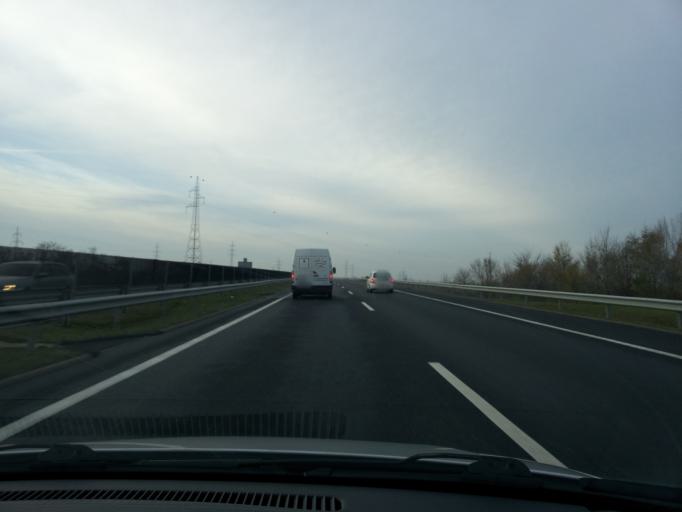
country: HU
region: Pest
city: Szazhalombatta
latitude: 47.3288
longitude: 18.8817
